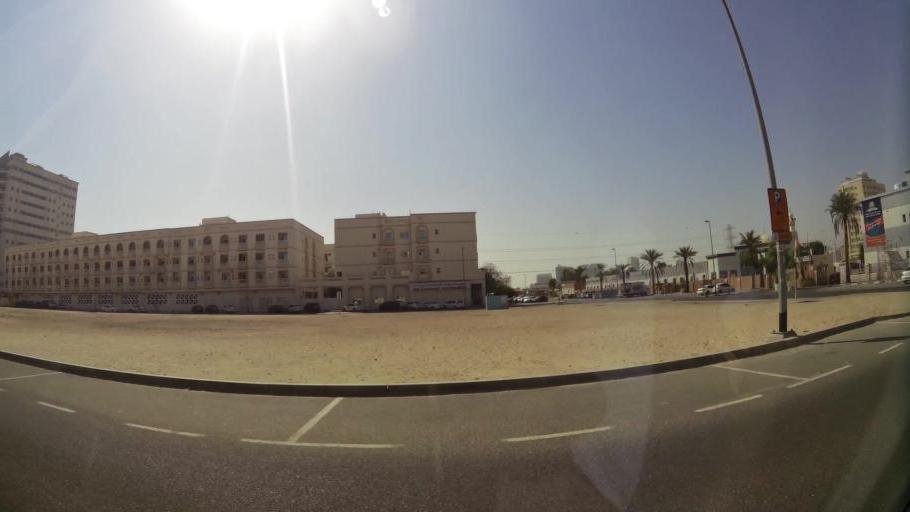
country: AE
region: Ash Shariqah
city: Sharjah
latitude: 25.2775
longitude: 55.3721
